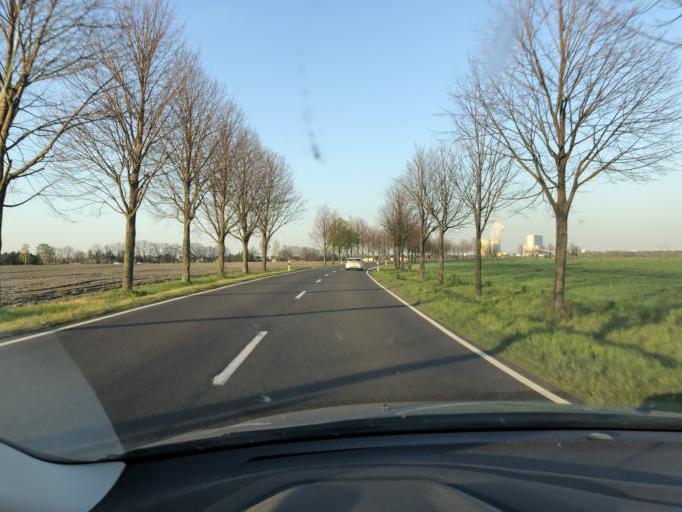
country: DE
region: Brandenburg
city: Spremberg
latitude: 51.5255
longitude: 14.3001
